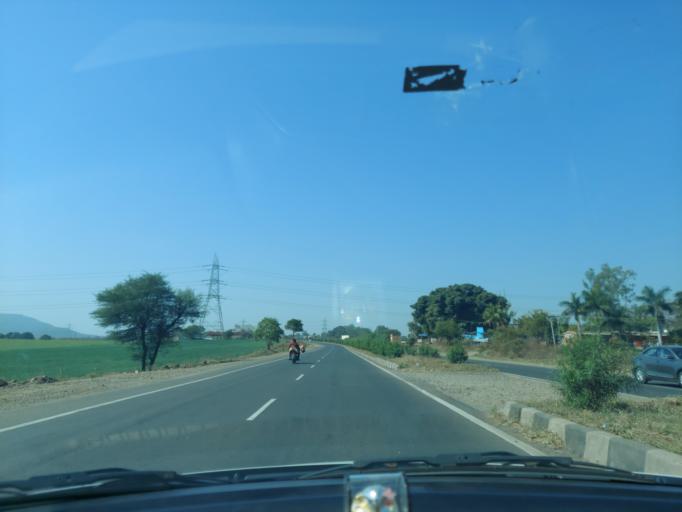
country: IN
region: Madhya Pradesh
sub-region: Indore
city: Manpur
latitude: 22.4226
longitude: 75.6041
